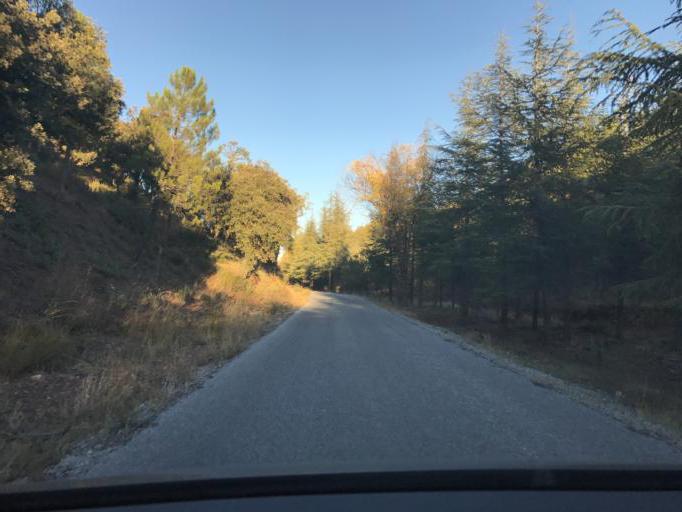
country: ES
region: Andalusia
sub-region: Provincia de Granada
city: Beas de Granada
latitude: 37.2910
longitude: -3.4899
